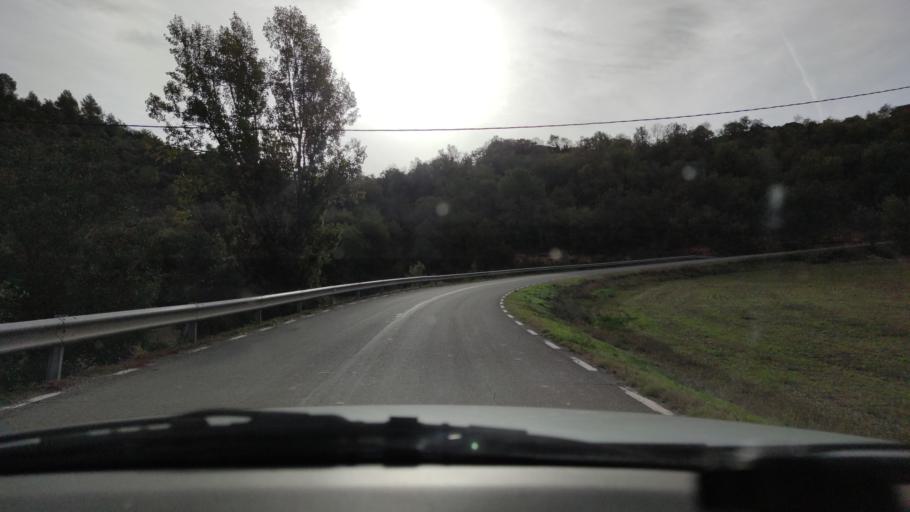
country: ES
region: Catalonia
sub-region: Provincia de Lleida
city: Ponts
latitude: 41.9187
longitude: 1.1143
